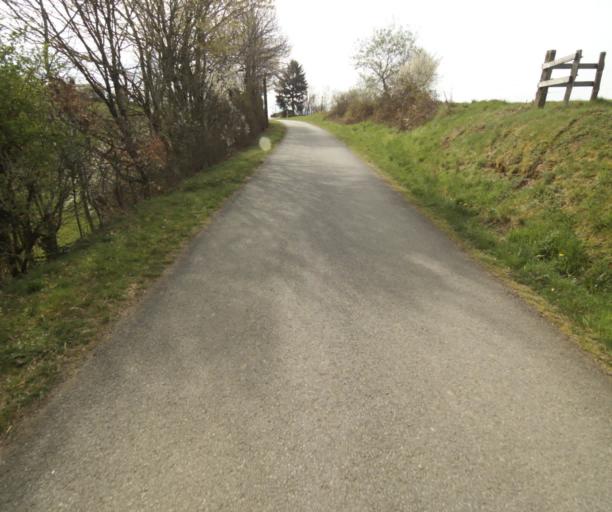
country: FR
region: Limousin
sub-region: Departement de la Correze
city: Correze
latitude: 45.3910
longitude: 1.8147
